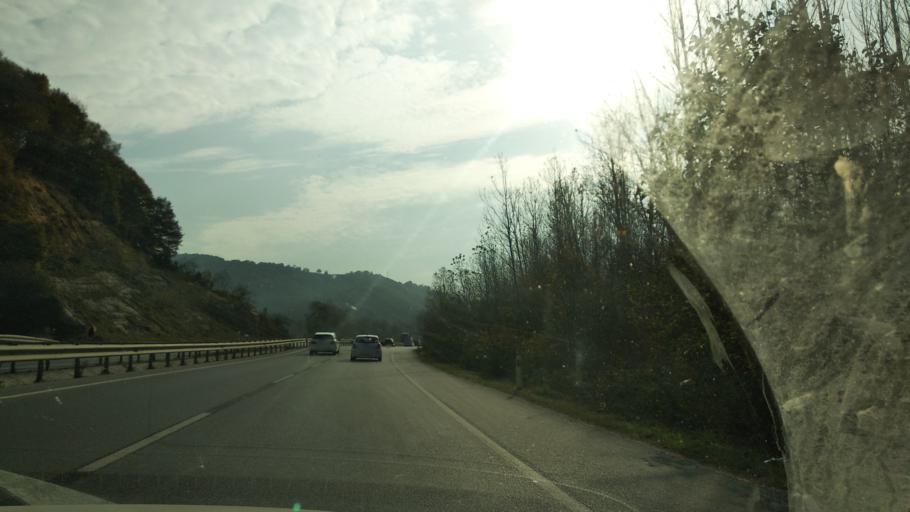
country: TR
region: Sakarya
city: Karasu
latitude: 41.0737
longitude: 30.6462
